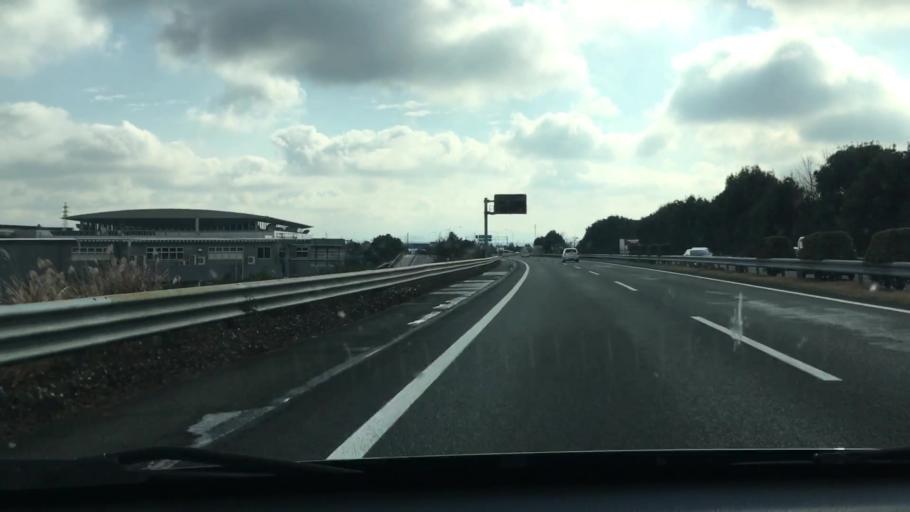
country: JP
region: Kumamoto
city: Kumamoto
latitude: 32.7967
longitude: 130.7900
